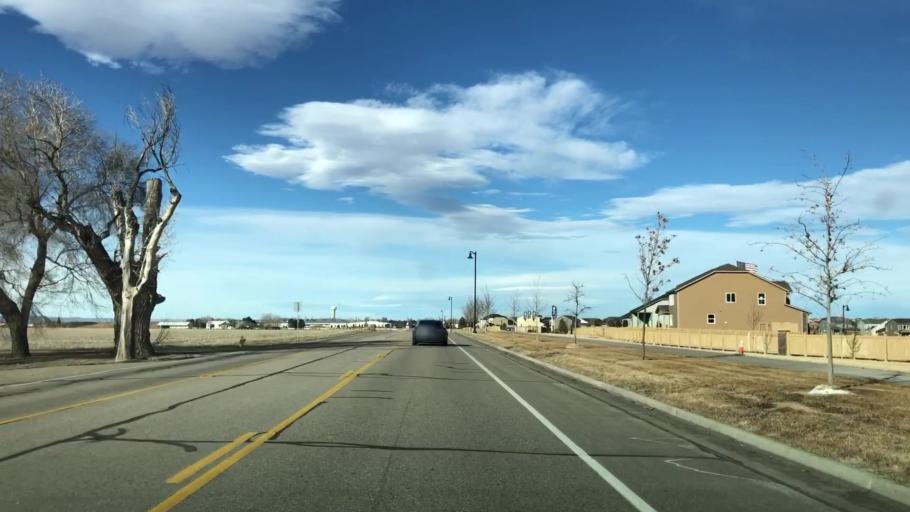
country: US
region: Colorado
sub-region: Weld County
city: Windsor
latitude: 40.5105
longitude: -104.9629
